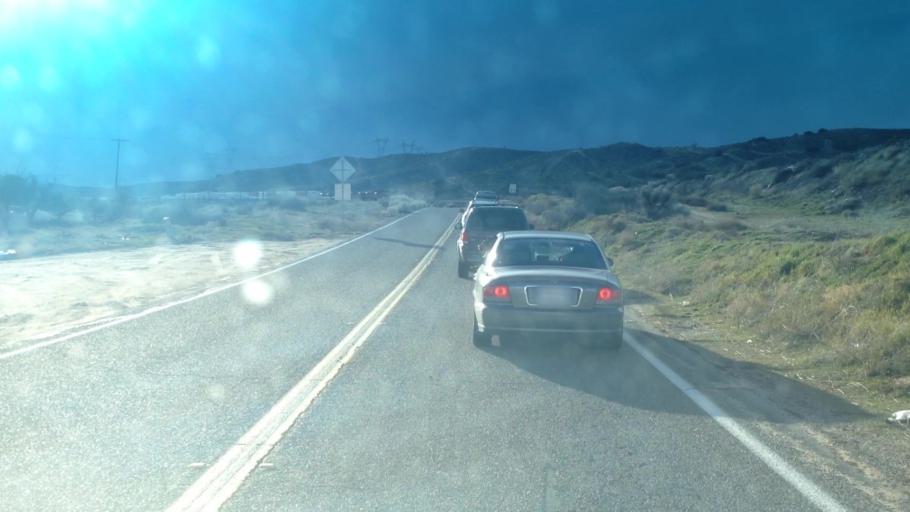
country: US
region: California
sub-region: San Bernardino County
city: Oak Hills
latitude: 34.3656
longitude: -117.3477
